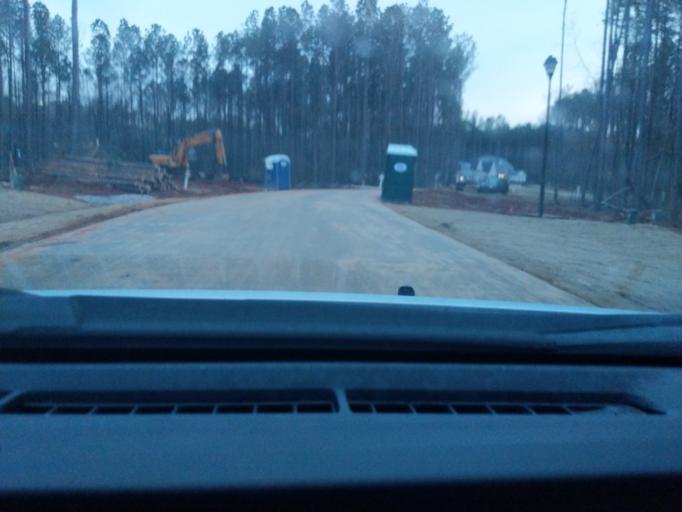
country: US
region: North Carolina
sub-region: Wake County
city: Garner
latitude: 35.7134
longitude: -78.6790
